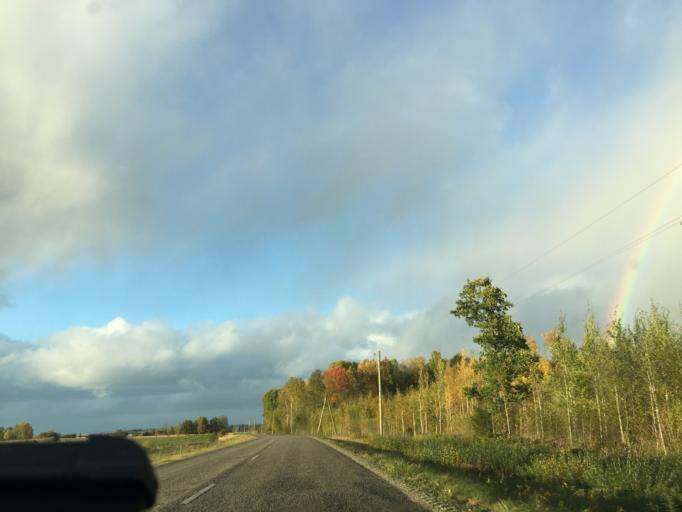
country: LV
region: Broceni
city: Broceni
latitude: 56.8690
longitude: 22.3822
